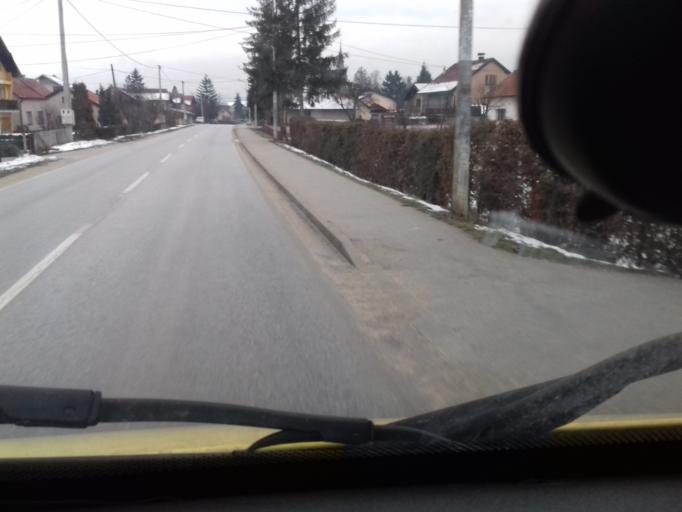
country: BA
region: Federation of Bosnia and Herzegovina
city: Vitez
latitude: 44.1621
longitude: 17.7800
